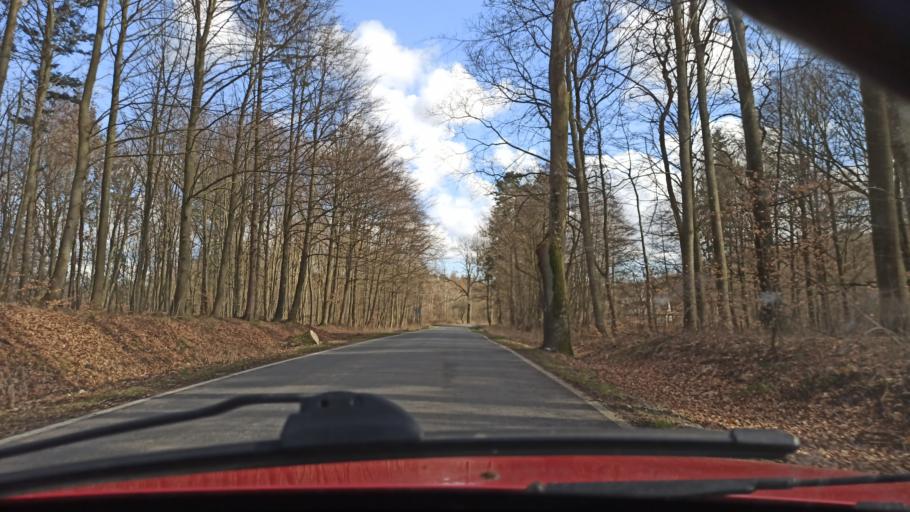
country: PL
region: Warmian-Masurian Voivodeship
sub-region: Powiat elblaski
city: Tolkmicko
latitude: 54.2801
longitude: 19.4782
